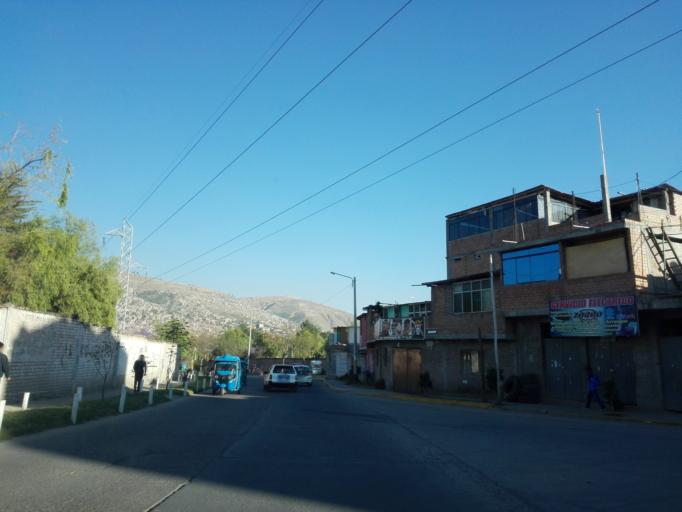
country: PE
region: Ayacucho
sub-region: Provincia de Huamanga
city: Ayacucho
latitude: -13.1507
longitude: -74.2191
